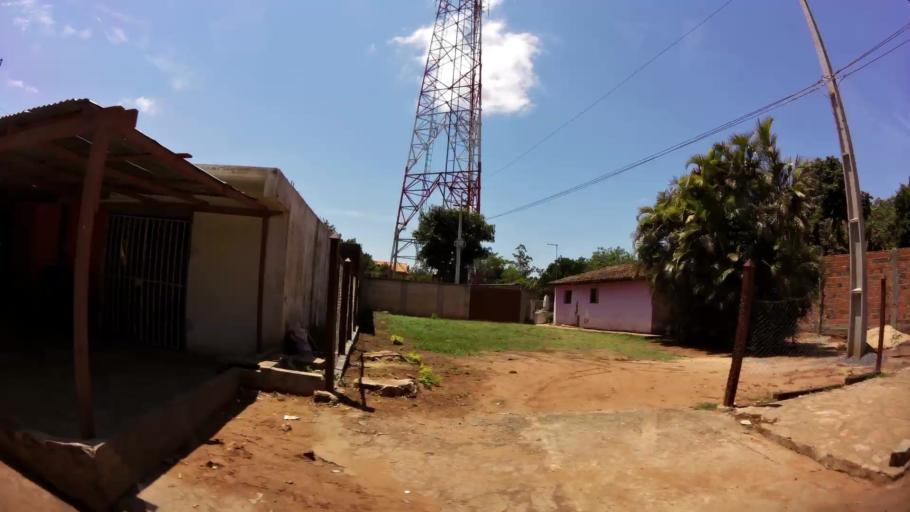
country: PY
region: Central
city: Nemby
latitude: -25.4027
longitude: -57.5299
